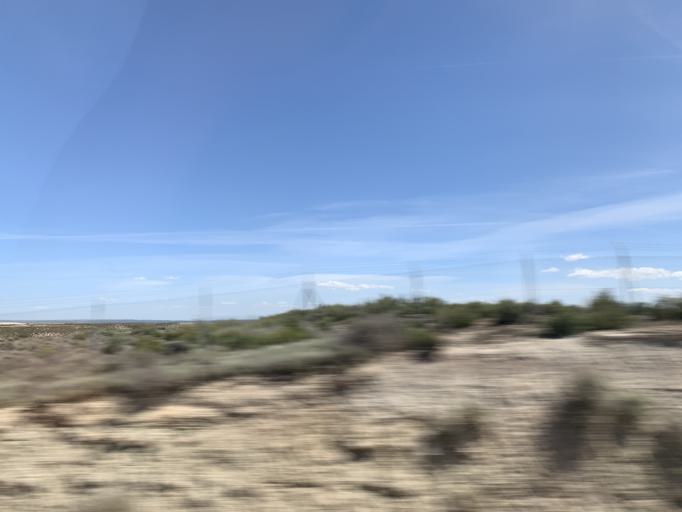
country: ES
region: Aragon
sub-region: Provincia de Huesca
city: Candasnos
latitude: 41.5249
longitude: 0.0167
